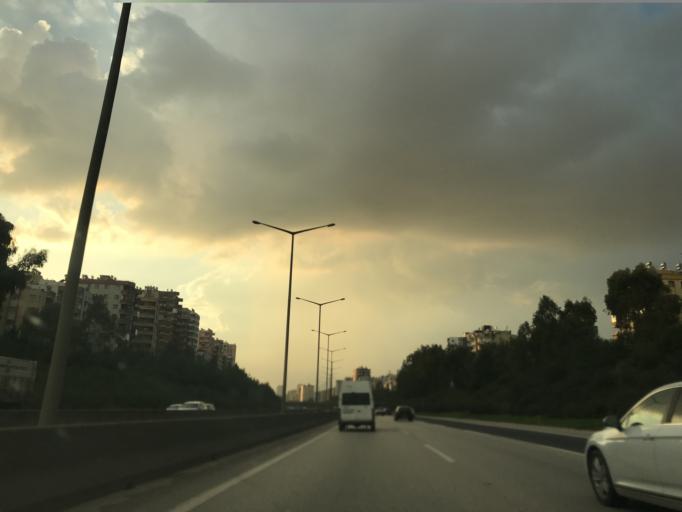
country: TR
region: Adana
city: Adana
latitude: 37.0320
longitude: 35.3065
